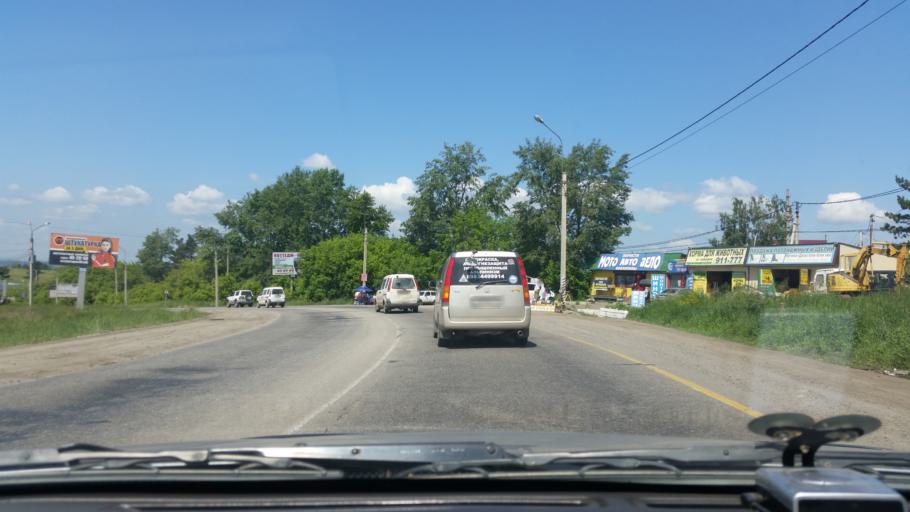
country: RU
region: Irkutsk
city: Smolenshchina
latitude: 52.2612
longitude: 104.1945
